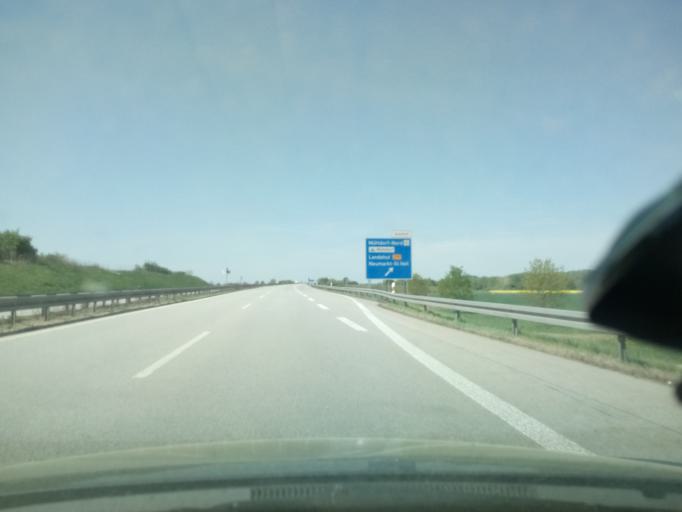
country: DE
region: Bavaria
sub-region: Upper Bavaria
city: Rohrbach
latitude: 48.2744
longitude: 12.5590
